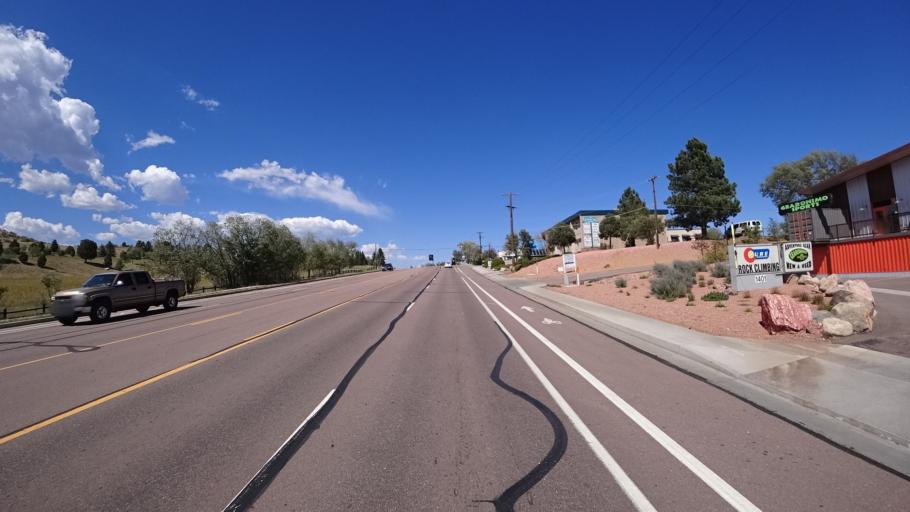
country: US
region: Colorado
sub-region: El Paso County
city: Colorado Springs
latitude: 38.8138
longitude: -104.8408
